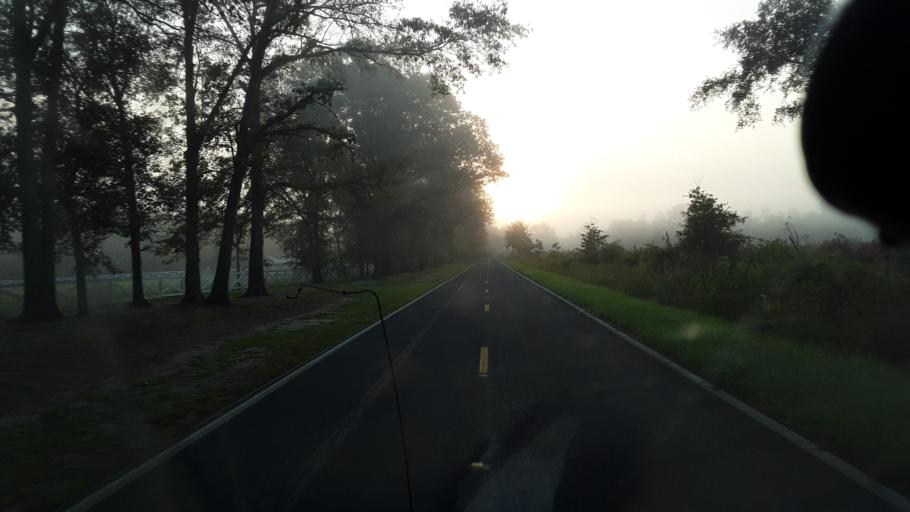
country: US
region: South Carolina
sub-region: Clarendon County
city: Manning
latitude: 33.7303
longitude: -80.0991
